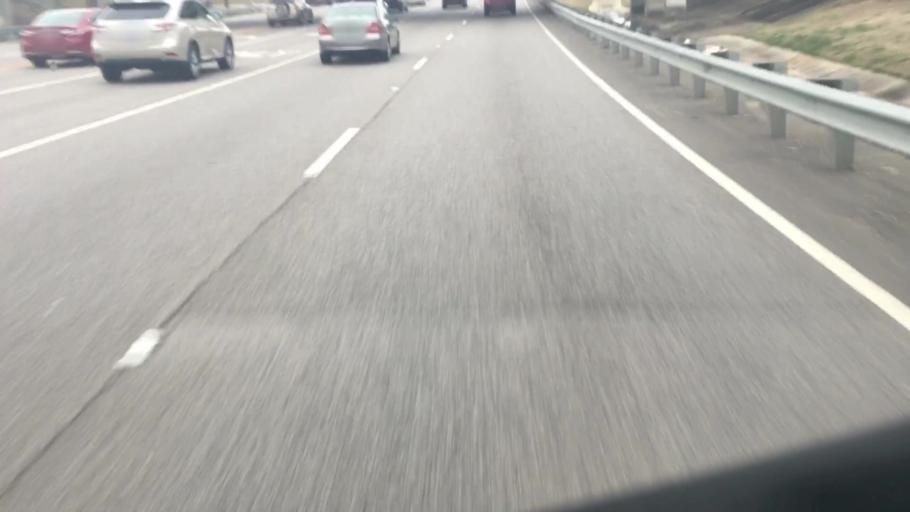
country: US
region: Alabama
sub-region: Shelby County
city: Helena
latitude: 33.3566
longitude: -86.8513
